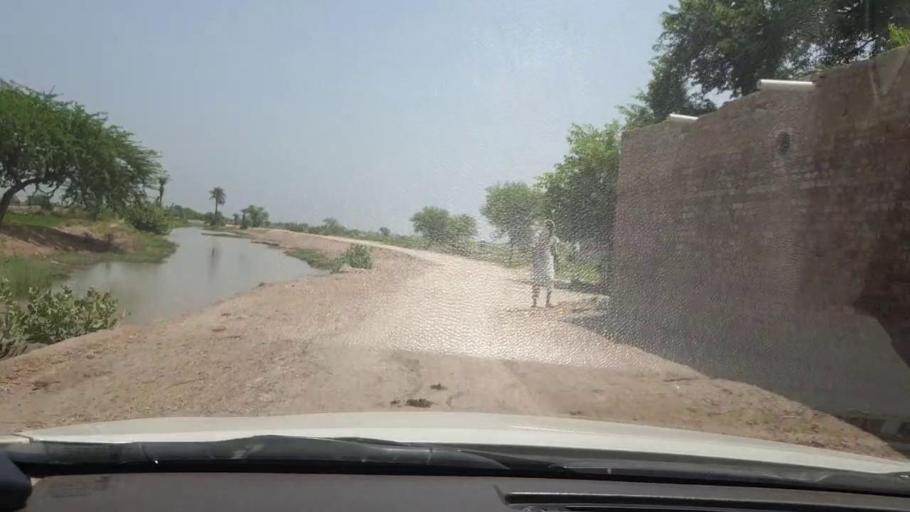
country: PK
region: Sindh
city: Garhi Yasin
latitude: 27.8960
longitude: 68.5395
